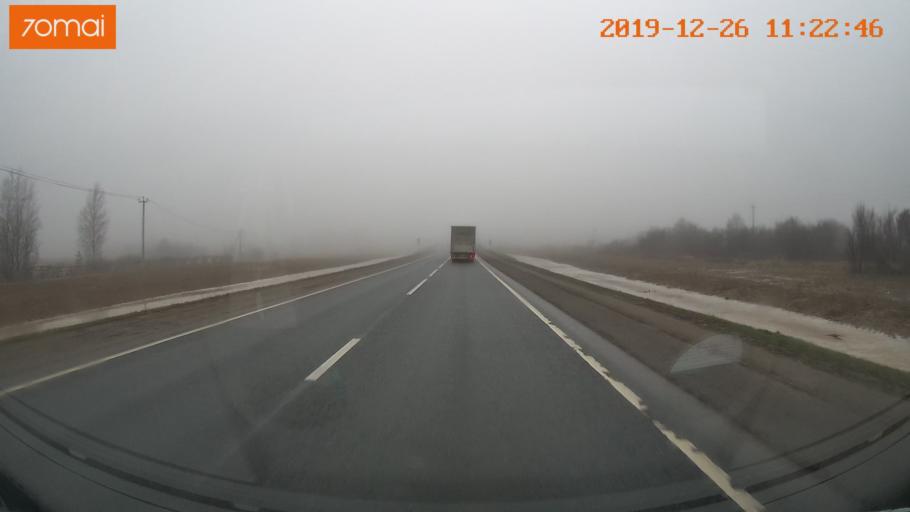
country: RU
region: Vologda
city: Chebsara
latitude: 59.1298
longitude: 38.9362
